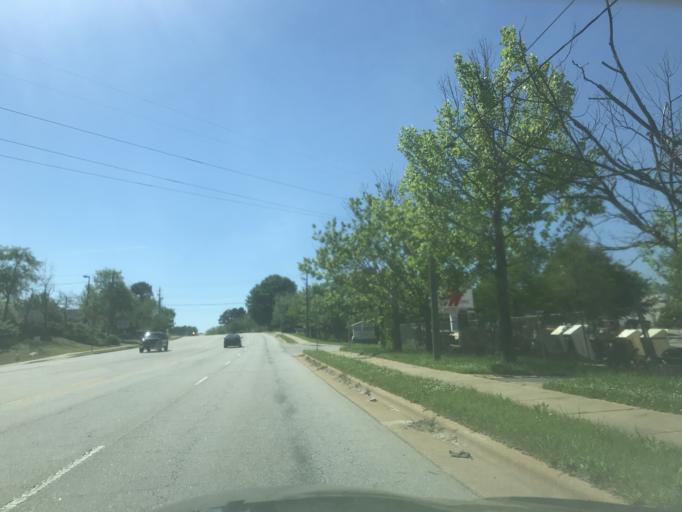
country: US
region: North Carolina
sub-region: Wake County
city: Garner
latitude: 35.7315
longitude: -78.6444
